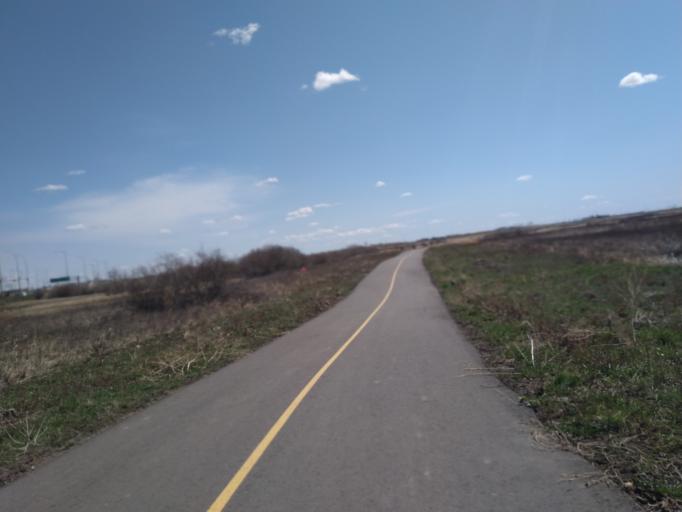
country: CA
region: Alberta
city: Chestermere
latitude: 51.0375
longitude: -113.9334
